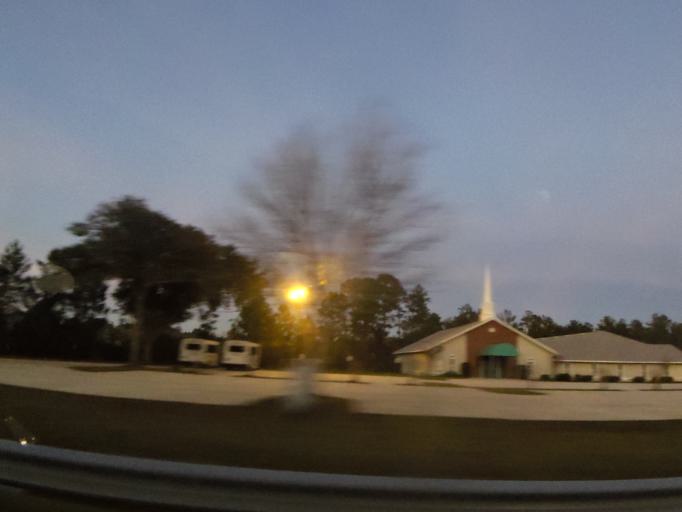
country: US
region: Florida
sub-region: Saint Johns County
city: Saint Augustine South
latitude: 29.8304
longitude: -81.3558
